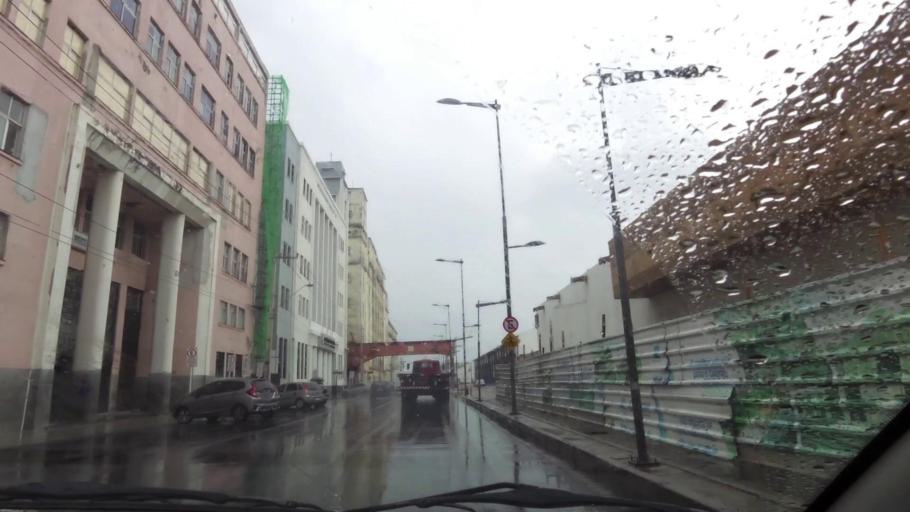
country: BR
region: Pernambuco
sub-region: Recife
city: Recife
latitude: -8.0603
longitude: -34.8706
